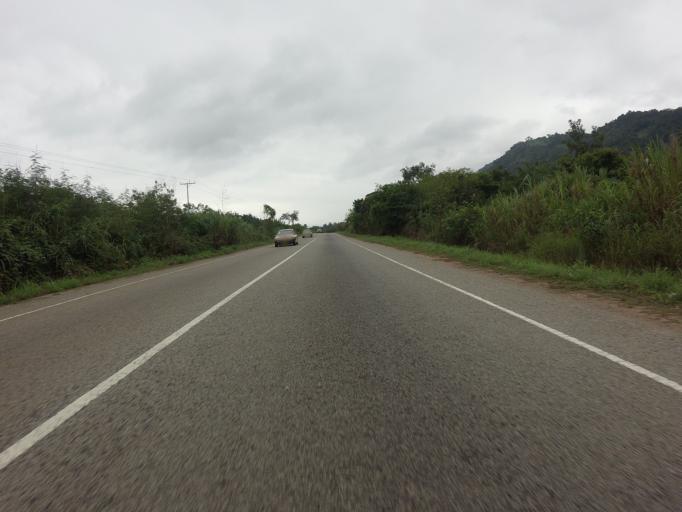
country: GH
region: Volta
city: Ho
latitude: 6.7423
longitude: 0.4803
